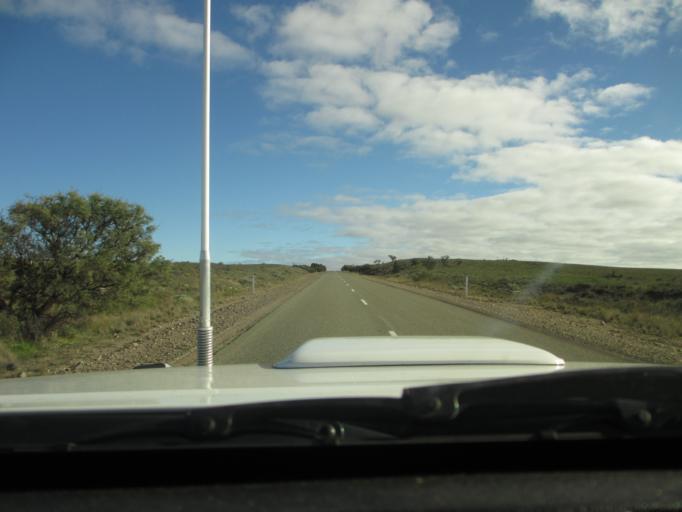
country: AU
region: South Australia
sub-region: Peterborough
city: Peterborough
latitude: -32.6245
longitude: 138.5831
